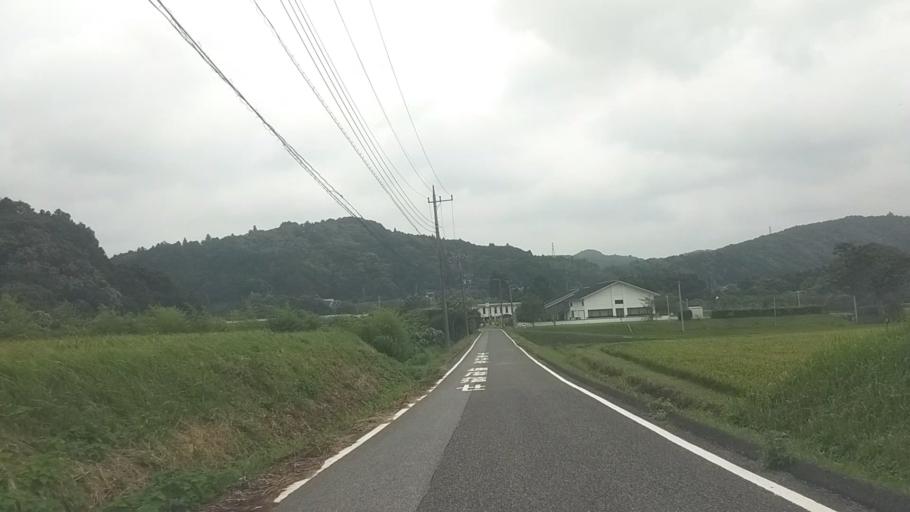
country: JP
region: Chiba
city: Kawaguchi
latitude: 35.2592
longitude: 140.0555
